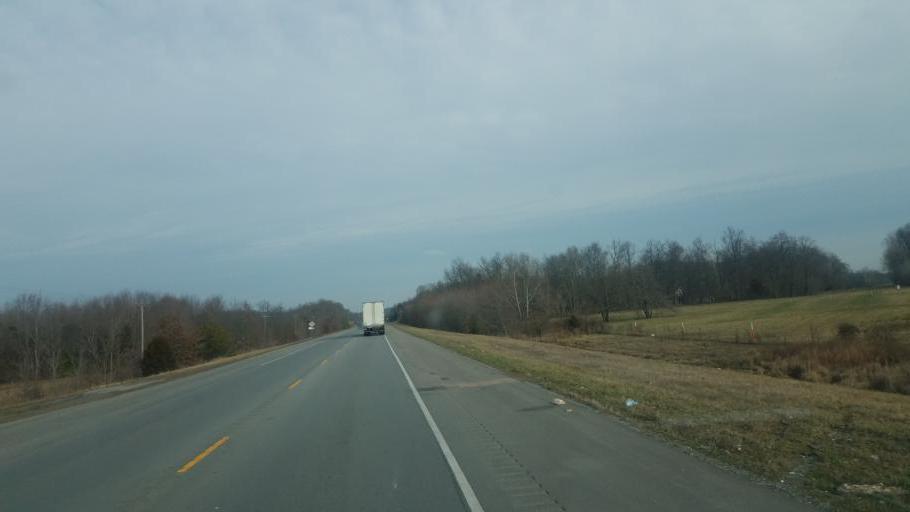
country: US
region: Kentucky
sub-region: Boyle County
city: Junction City
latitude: 37.5491
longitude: -84.8012
